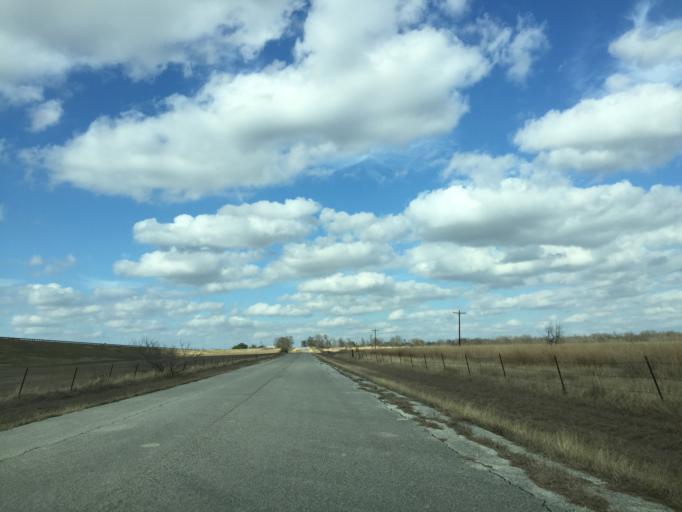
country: US
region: Texas
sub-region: Williamson County
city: Granger
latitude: 30.7124
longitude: -97.3229
